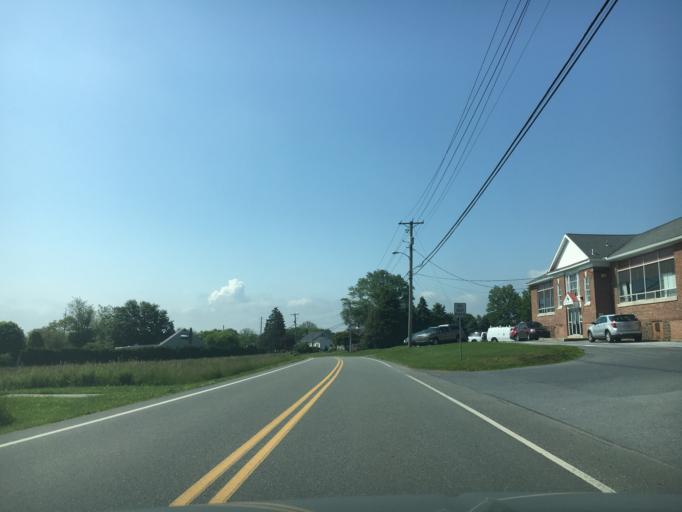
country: US
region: Pennsylvania
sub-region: Berks County
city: New Berlinville
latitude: 40.3418
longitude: -75.6279
